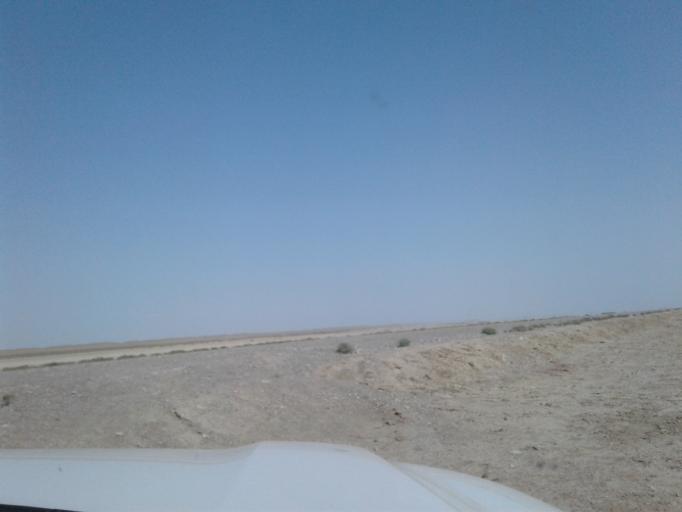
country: TM
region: Balkan
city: Gumdag
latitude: 38.3584
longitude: 54.5248
